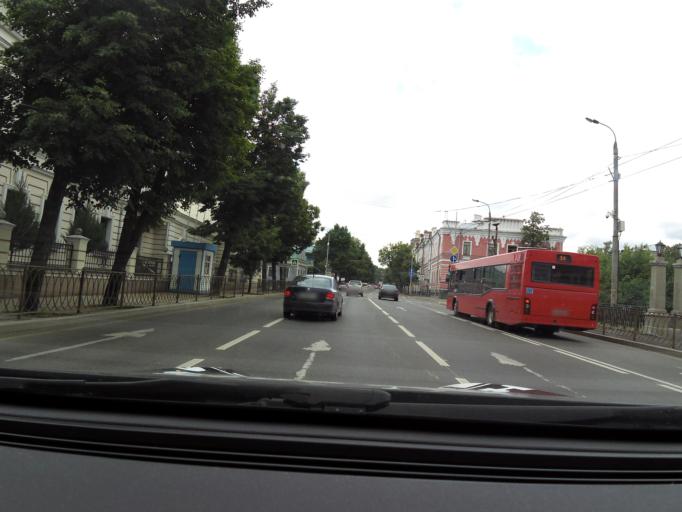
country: RU
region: Tatarstan
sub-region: Gorod Kazan'
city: Kazan
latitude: 55.7937
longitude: 49.1340
